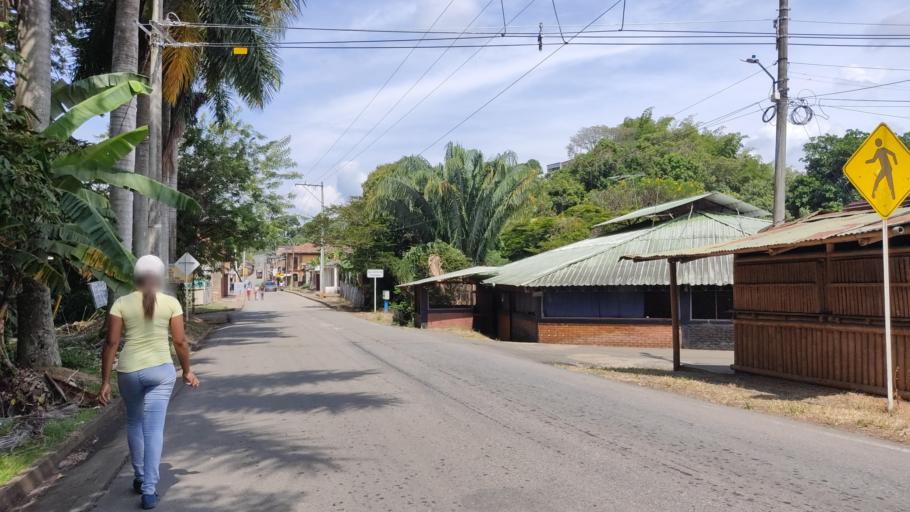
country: CO
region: Cauca
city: Buenos Aires
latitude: 3.1303
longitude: -76.5933
